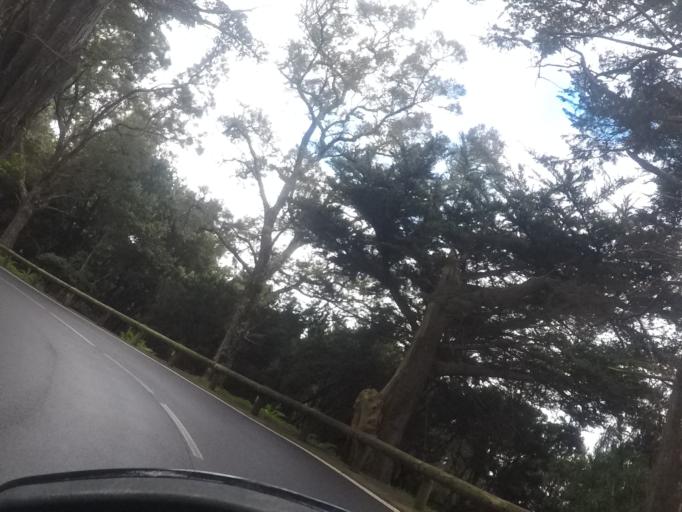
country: ES
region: Canary Islands
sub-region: Provincia de Santa Cruz de Tenerife
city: Tegueste
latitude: 28.5256
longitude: -16.2884
